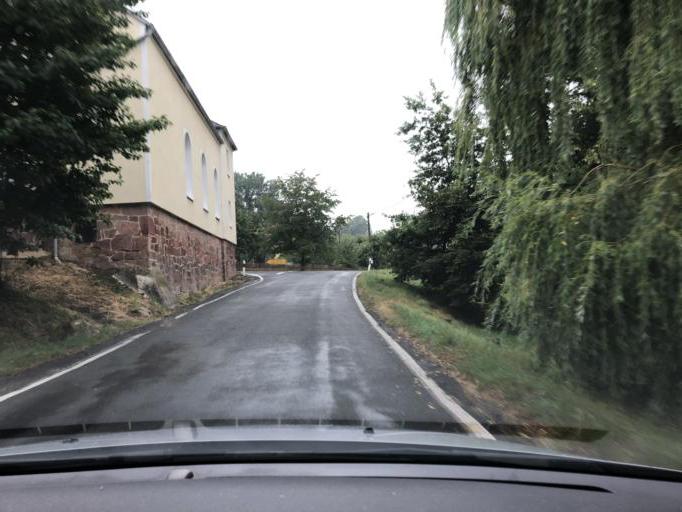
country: DE
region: Saxony
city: Narsdorf
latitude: 51.0007
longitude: 12.6795
